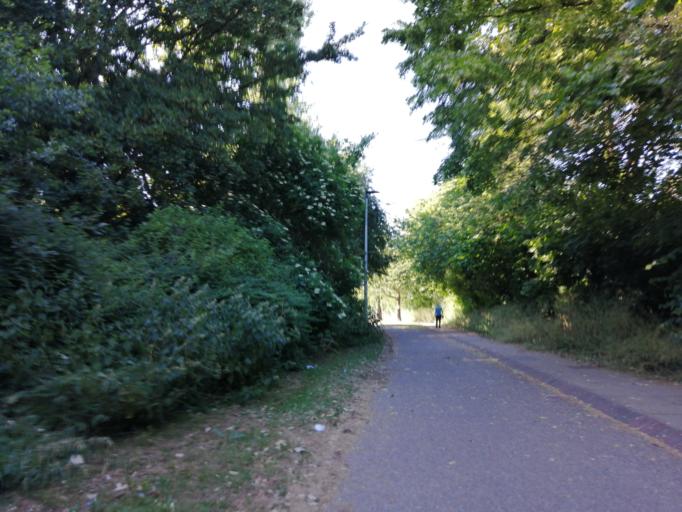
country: GB
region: England
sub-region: Peterborough
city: Peterborough
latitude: 52.5869
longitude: -0.2660
